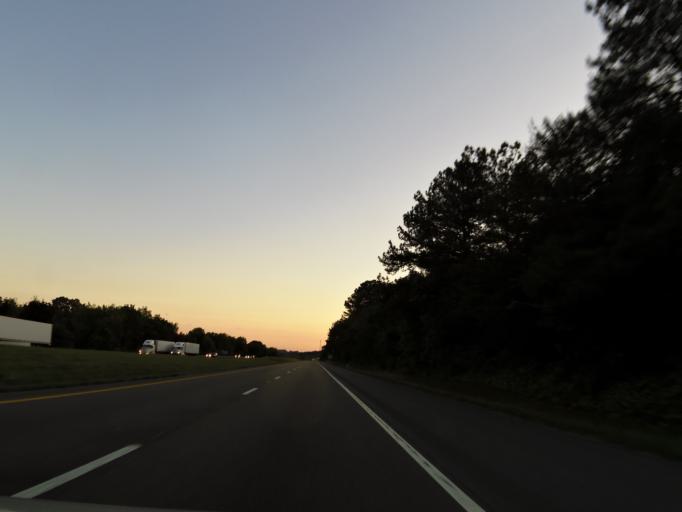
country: US
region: Tennessee
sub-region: Jefferson County
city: White Pine
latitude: 36.1536
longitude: -83.2422
